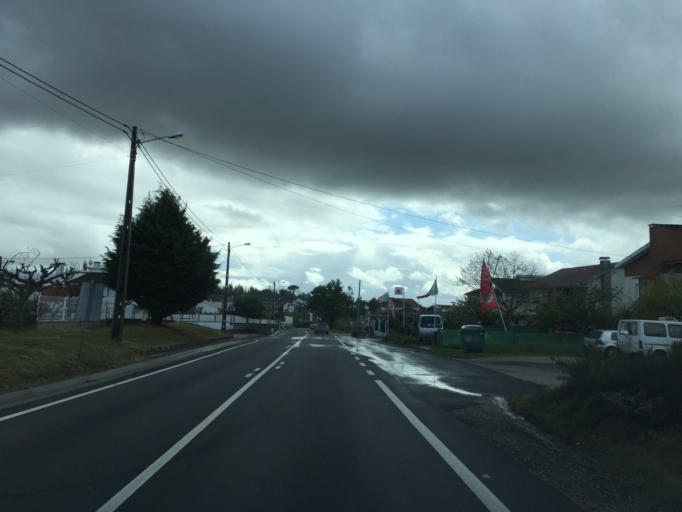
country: PT
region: Coimbra
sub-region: Oliveira do Hospital
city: Oliveira do Hospital
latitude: 40.3176
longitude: -7.8885
